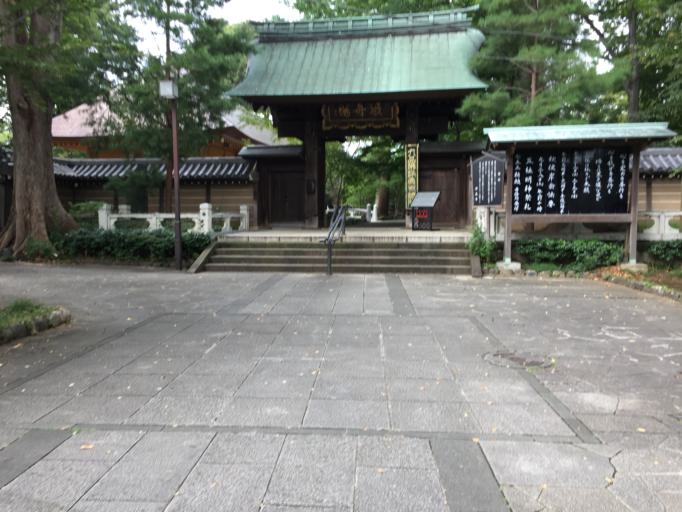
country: JP
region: Tokyo
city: Tokyo
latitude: 35.6071
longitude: 139.6616
